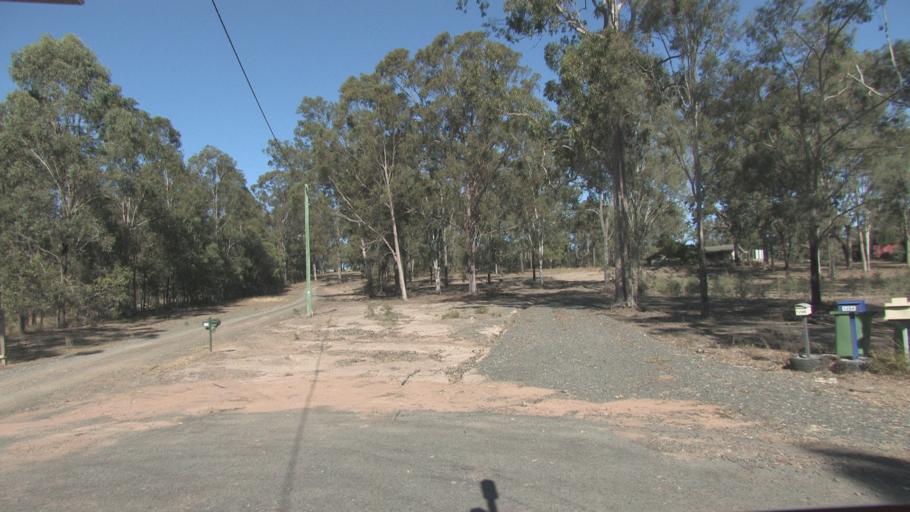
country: AU
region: Queensland
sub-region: Logan
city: Cedar Vale
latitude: -27.8665
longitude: 153.0268
